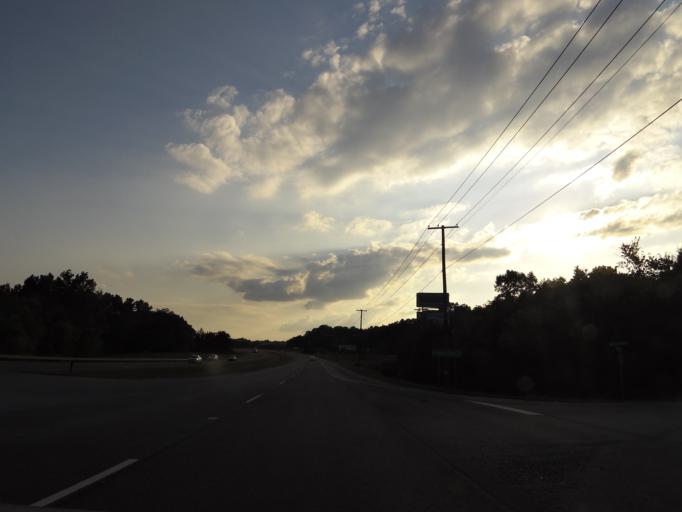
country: US
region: Tennessee
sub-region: Knox County
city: Mascot
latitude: 36.0355
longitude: -83.8402
